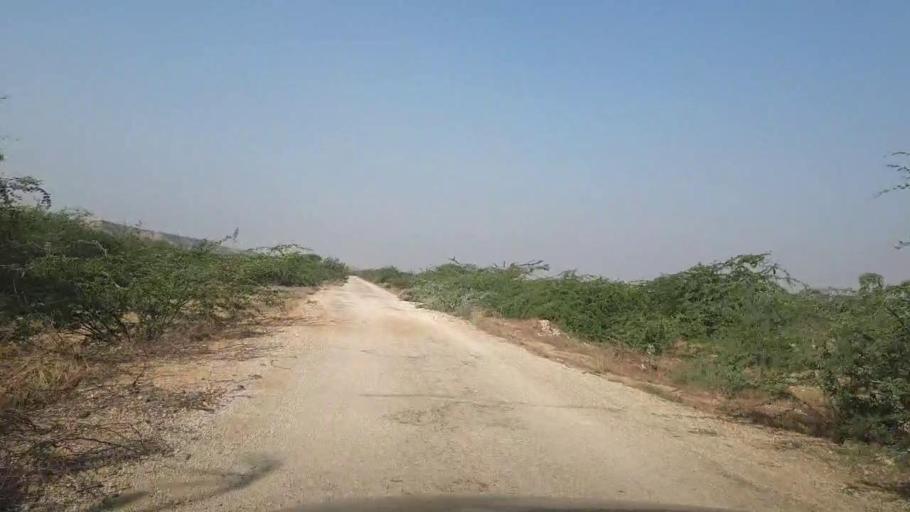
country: PK
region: Sindh
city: Gharo
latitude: 25.0516
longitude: 67.5553
